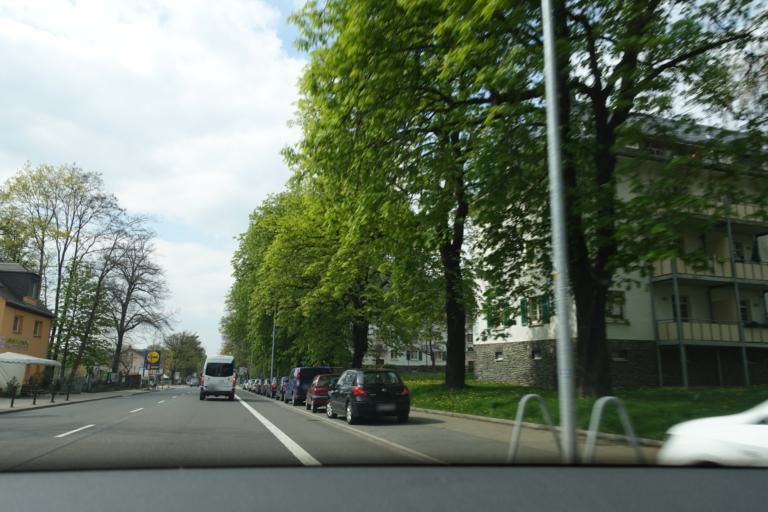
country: DE
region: Saxony
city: Chemnitz
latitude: 50.8178
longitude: 12.9469
